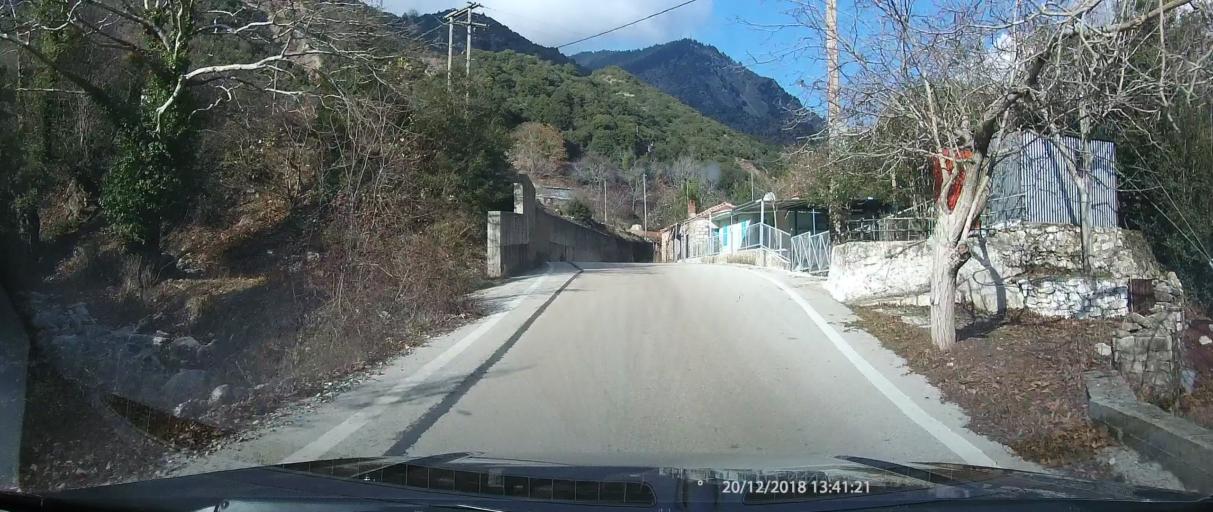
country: GR
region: West Greece
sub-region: Nomos Aitolias kai Akarnanias
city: Thermo
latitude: 38.6481
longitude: 21.6147
